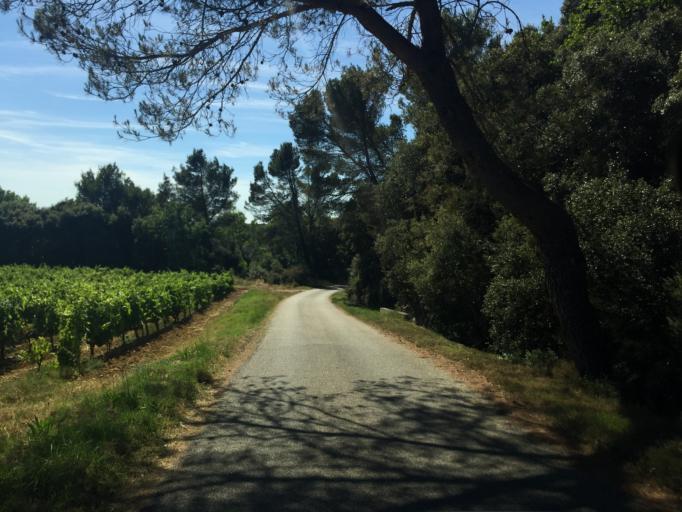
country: FR
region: Provence-Alpes-Cote d'Azur
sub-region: Departement du Vaucluse
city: Chateauneuf-du-Pape
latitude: 44.0845
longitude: 4.8077
